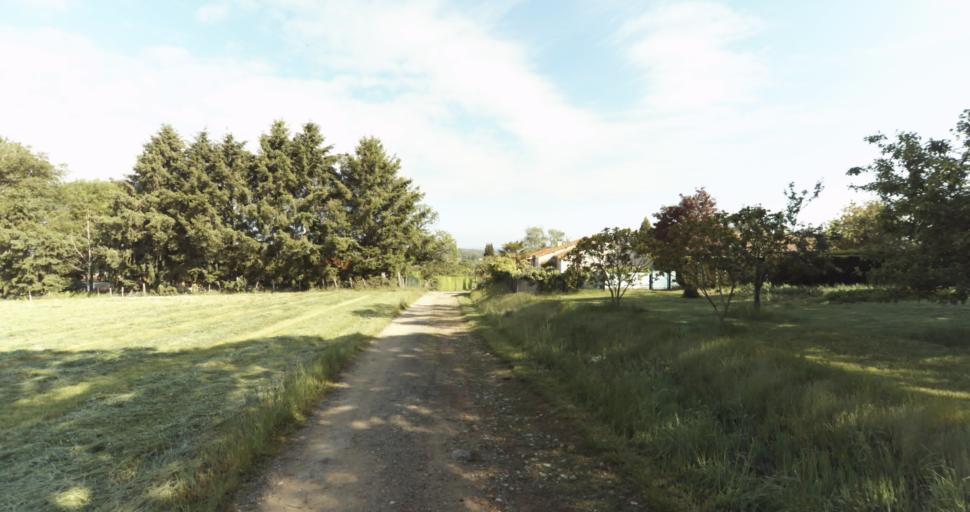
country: FR
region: Limousin
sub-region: Departement de la Haute-Vienne
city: Solignac
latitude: 45.7244
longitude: 1.2403
